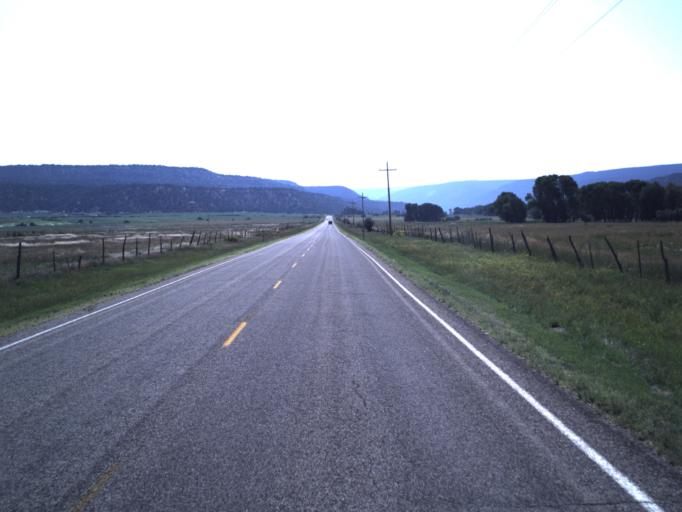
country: US
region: Utah
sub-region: Duchesne County
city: Duchesne
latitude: 40.3418
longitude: -110.6934
